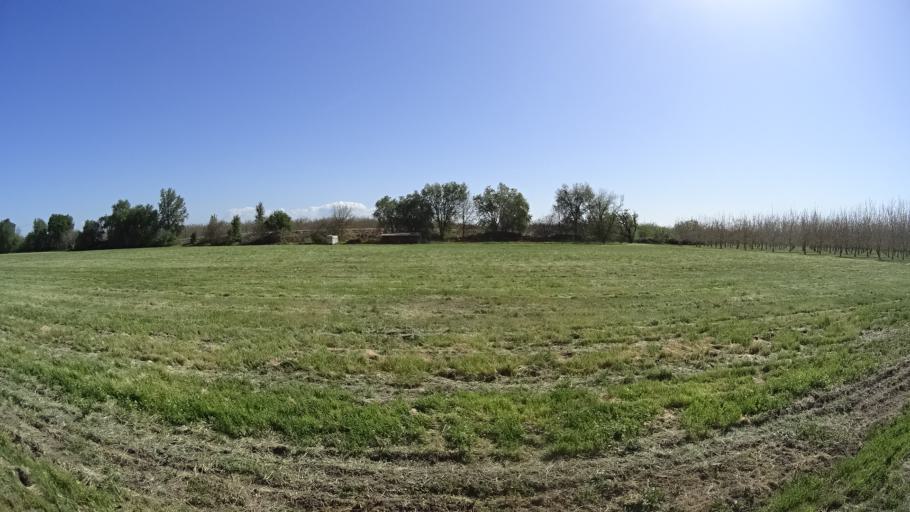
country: US
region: California
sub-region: Glenn County
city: Hamilton City
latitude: 39.7199
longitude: -122.0112
